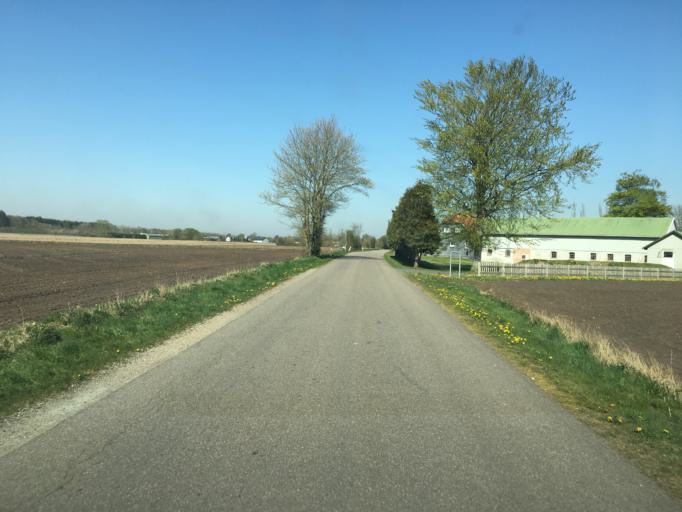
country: DK
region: South Denmark
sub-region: Aabenraa Kommune
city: Rodekro
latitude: 55.0839
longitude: 9.2667
